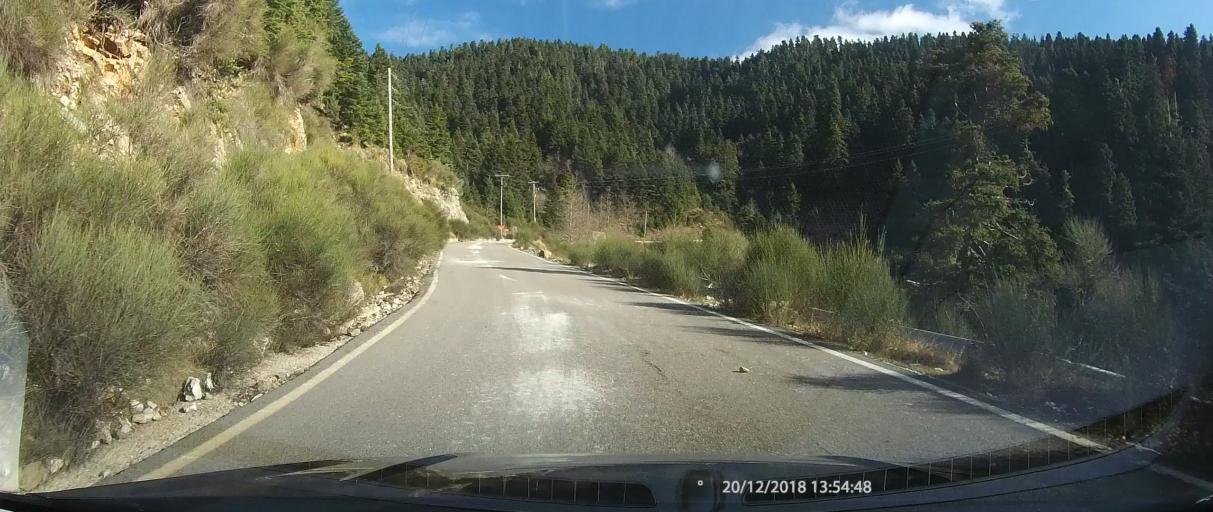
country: GR
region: West Greece
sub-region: Nomos Aitolias kai Akarnanias
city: Paravola
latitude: 38.7127
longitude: 21.6119
